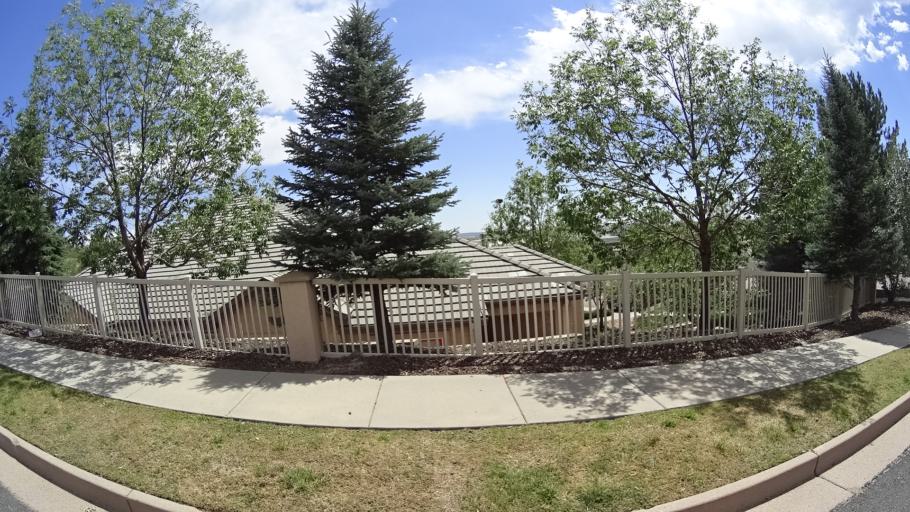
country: US
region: Colorado
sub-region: El Paso County
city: Stratmoor
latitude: 38.7681
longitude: -104.8169
